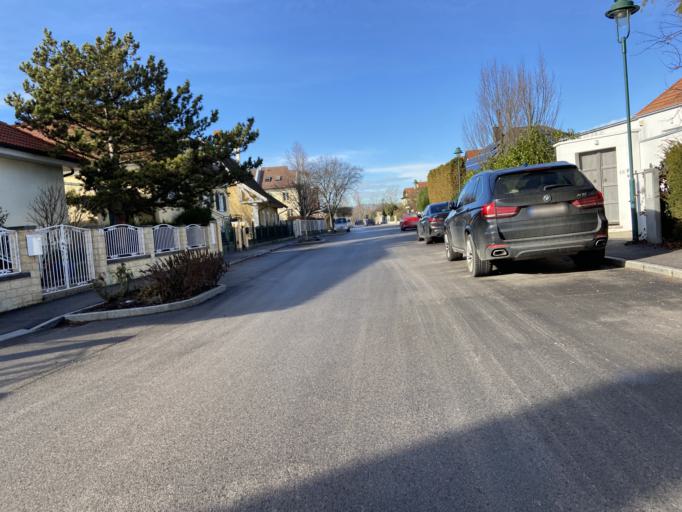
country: AT
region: Lower Austria
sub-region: Politischer Bezirk Modling
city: Laxenburg
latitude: 48.0724
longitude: 16.3525
